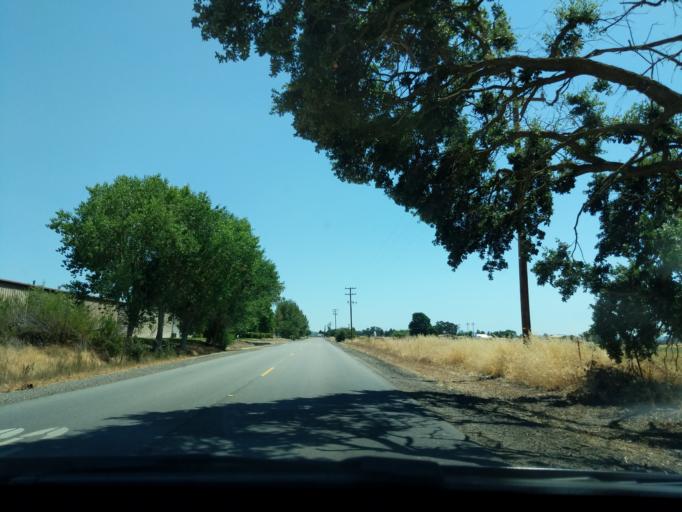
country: US
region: California
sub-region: San Luis Obispo County
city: Paso Robles
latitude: 35.6767
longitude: -120.6409
